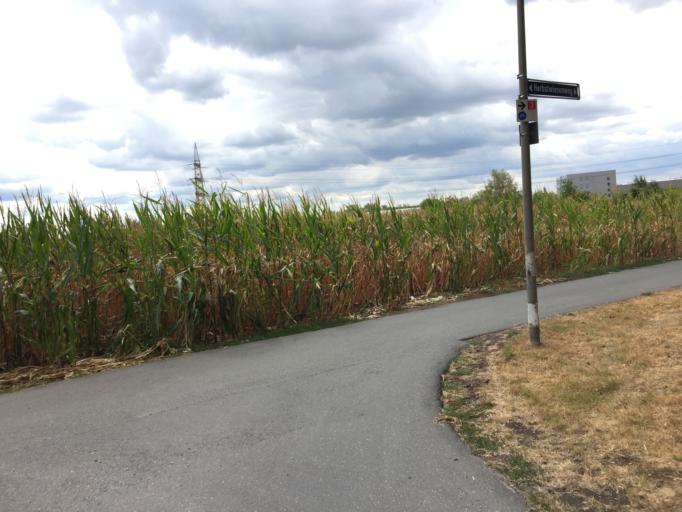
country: DE
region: Bavaria
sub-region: Regierungsbezirk Mittelfranken
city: Erlangen
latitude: 49.5600
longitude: 11.0025
